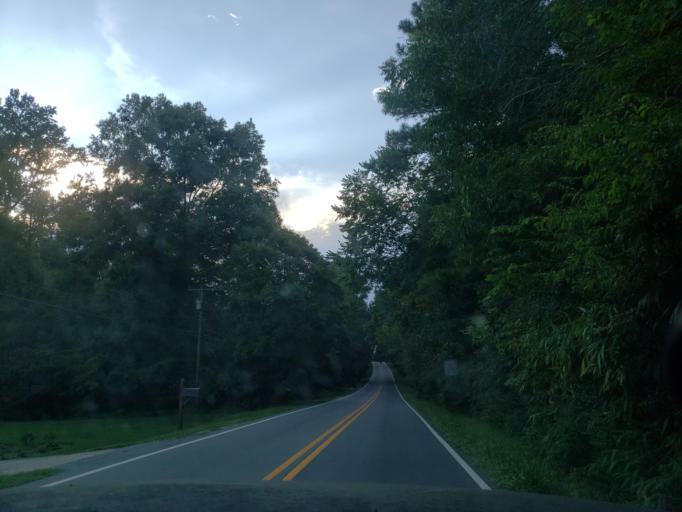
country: US
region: North Carolina
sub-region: Durham County
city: Durham
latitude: 35.9880
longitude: -78.9654
